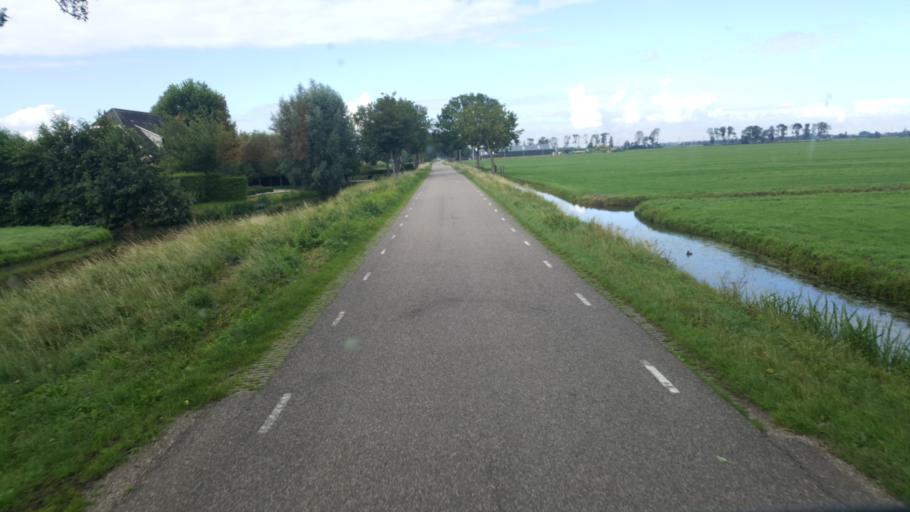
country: NL
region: South Holland
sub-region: Gemeente Hardinxveld-Giessendam
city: Neder-Hardinxveld
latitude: 51.8646
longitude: 4.8251
